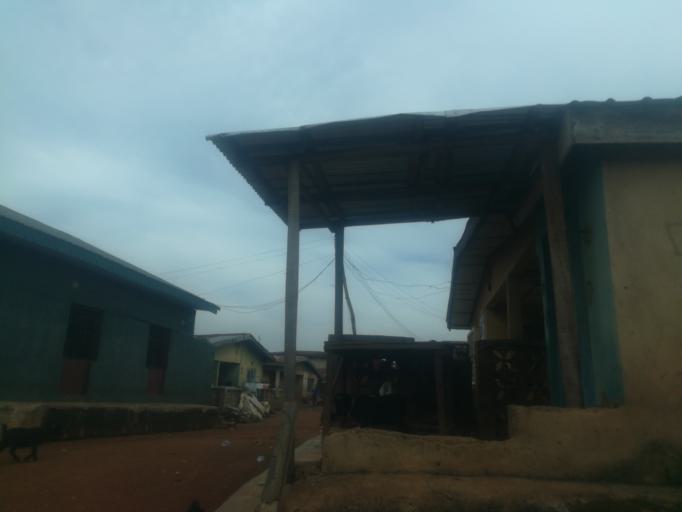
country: NG
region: Oyo
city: Ibadan
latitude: 7.3774
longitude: 3.9385
